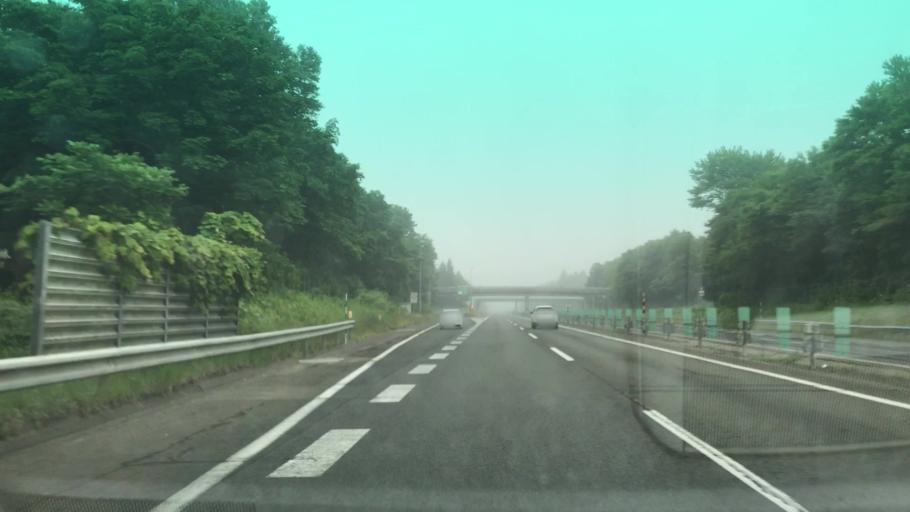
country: JP
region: Hokkaido
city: Chitose
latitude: 42.8146
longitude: 141.6199
